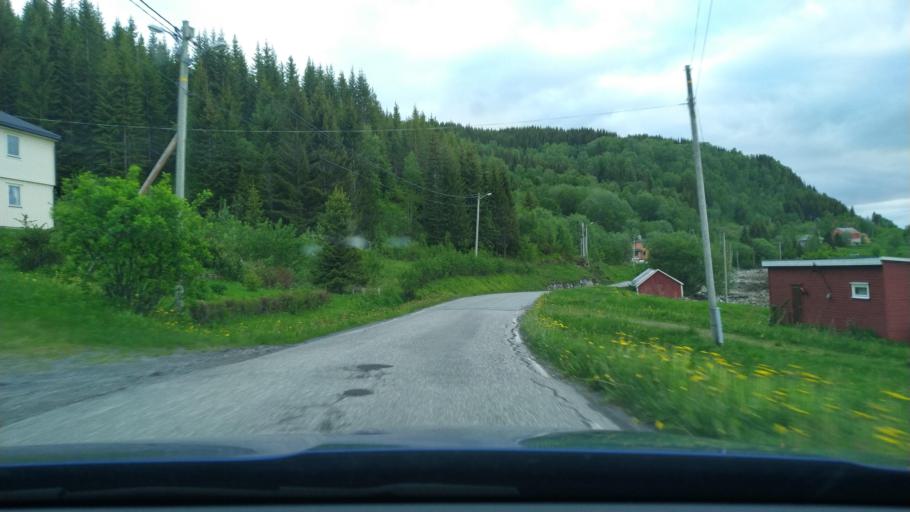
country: NO
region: Troms
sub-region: Lenvik
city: Finnsnes
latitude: 69.1353
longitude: 17.8987
